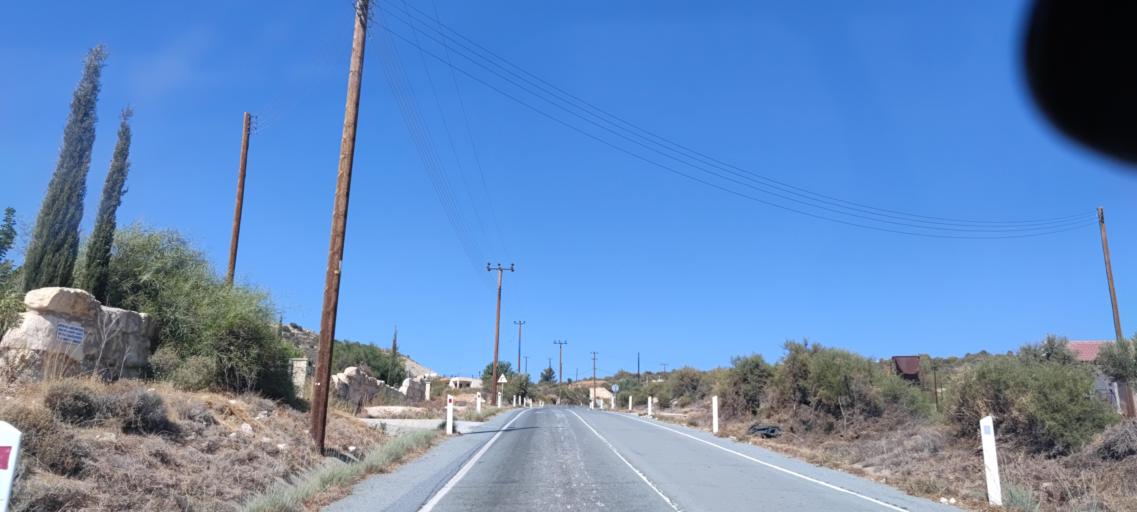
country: CY
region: Limassol
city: Mouttagiaka
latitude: 34.7474
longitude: 33.0577
